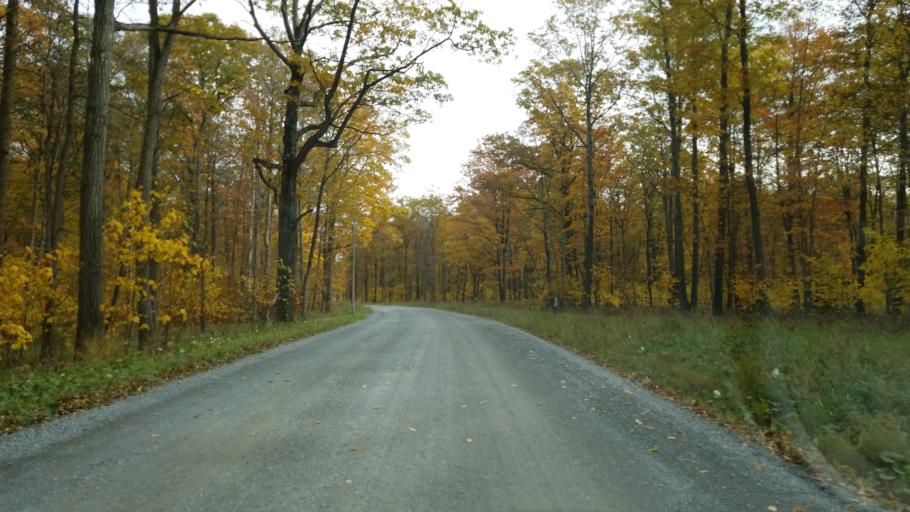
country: US
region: Pennsylvania
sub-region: Clearfield County
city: Clearfield
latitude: 41.1384
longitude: -78.5082
